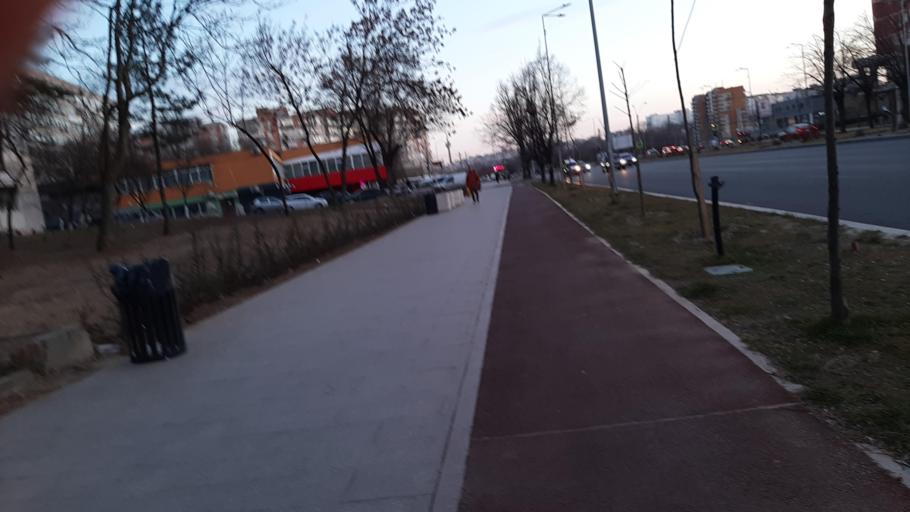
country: RO
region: Galati
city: Galati
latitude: 45.4292
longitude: 28.0249
